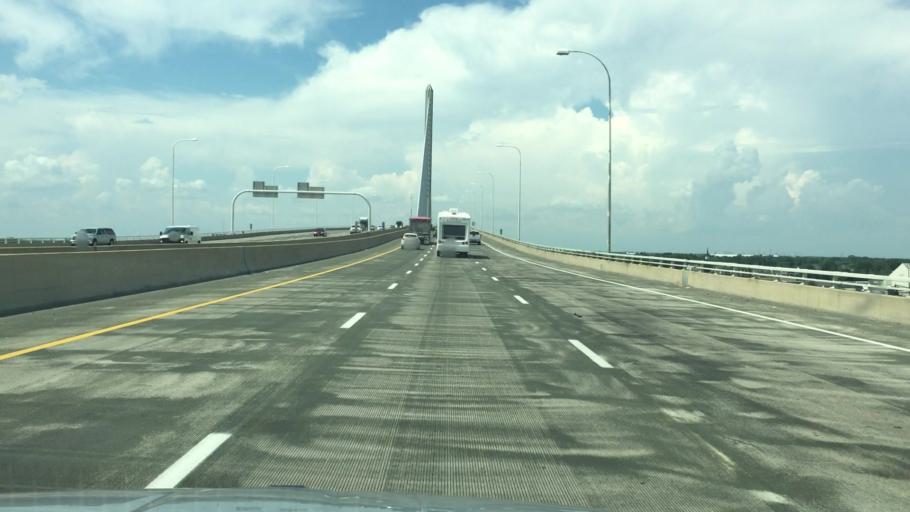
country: US
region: Ohio
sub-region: Lucas County
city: Oregon
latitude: 41.6569
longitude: -83.5086
